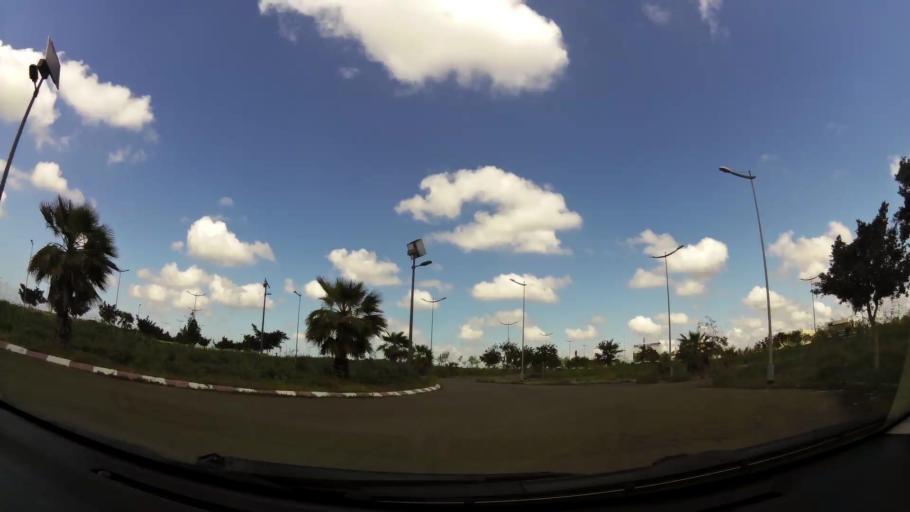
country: MA
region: Grand Casablanca
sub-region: Nouaceur
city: Dar Bouazza
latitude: 33.4227
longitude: -7.8253
